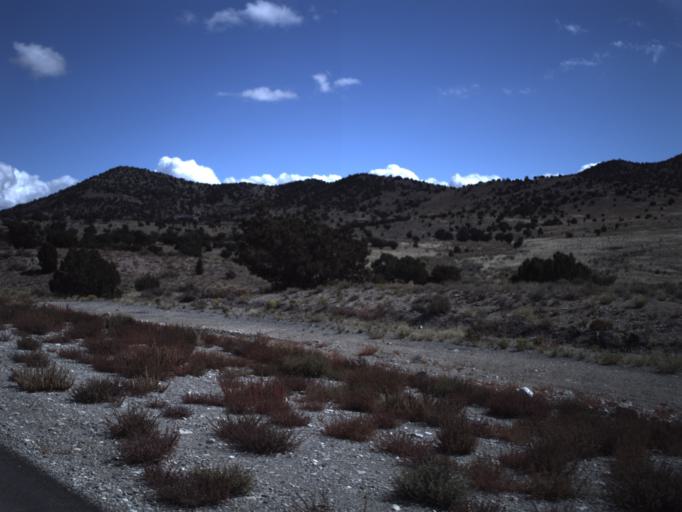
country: US
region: Utah
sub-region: Beaver County
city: Milford
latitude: 38.5144
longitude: -113.5649
